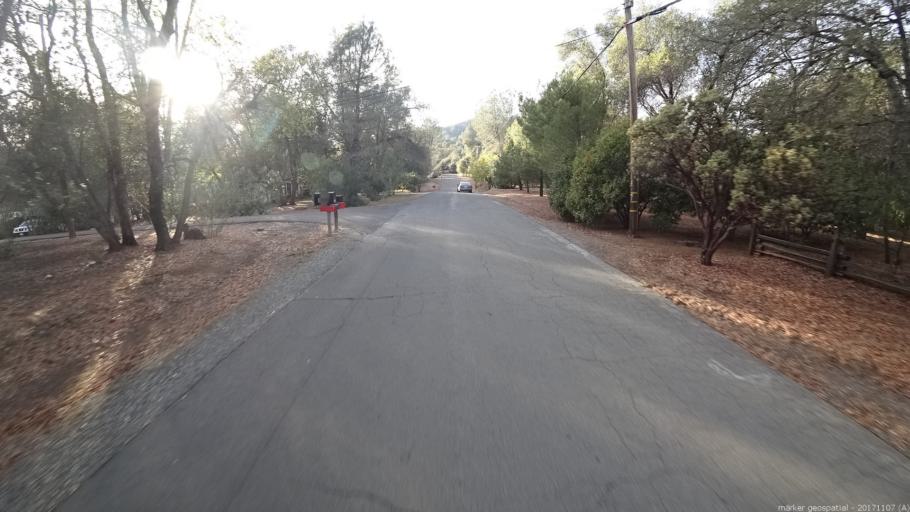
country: US
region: California
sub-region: Shasta County
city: Shasta
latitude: 40.5308
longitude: -122.4796
